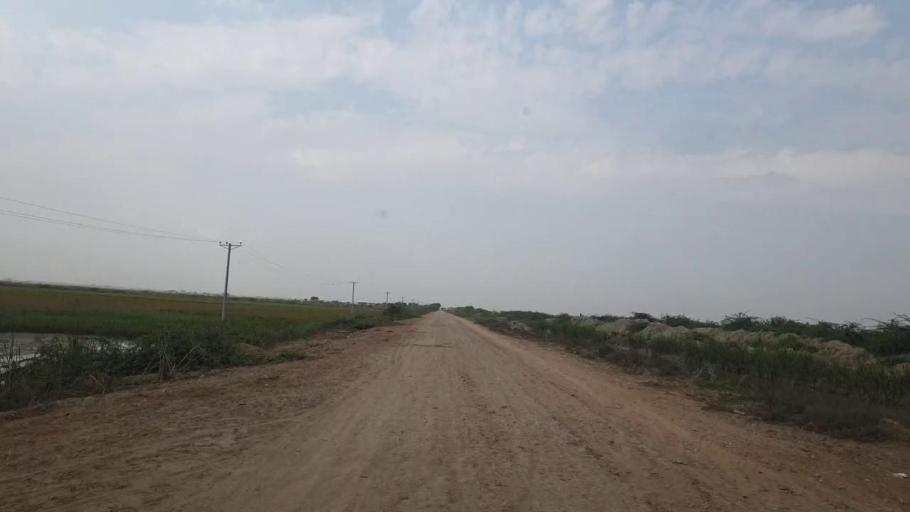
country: PK
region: Sindh
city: Kario
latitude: 24.6169
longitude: 68.5860
